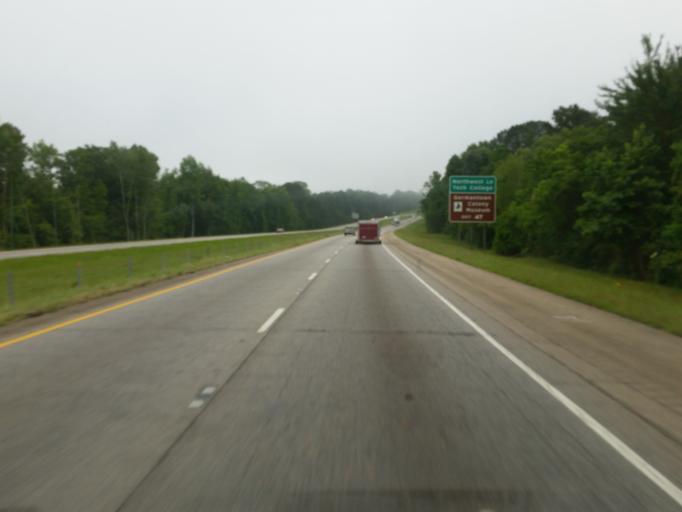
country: US
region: Louisiana
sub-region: Webster Parish
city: Minden
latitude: 32.5941
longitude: -93.3143
